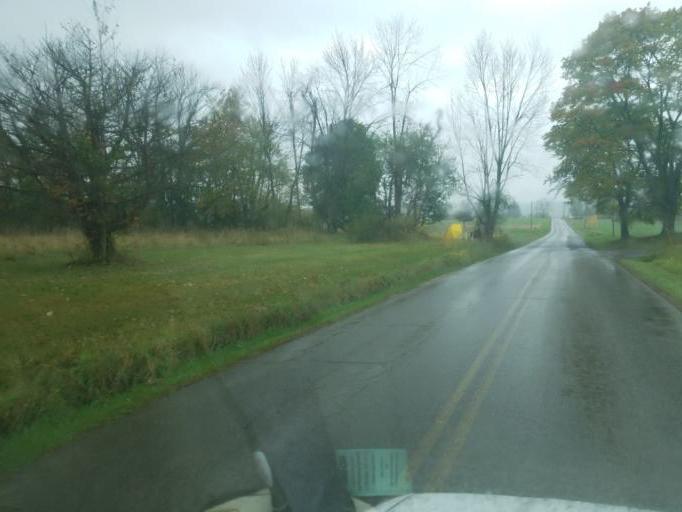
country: US
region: Ohio
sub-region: Wayne County
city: Shreve
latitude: 40.6569
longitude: -82.0182
